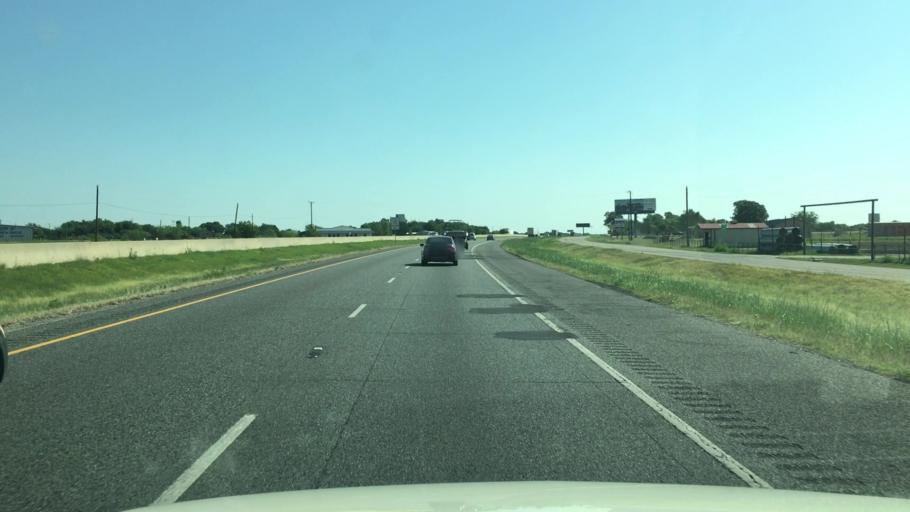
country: US
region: Texas
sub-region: Hunt County
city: Caddo Mills
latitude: 33.0498
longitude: -96.1741
